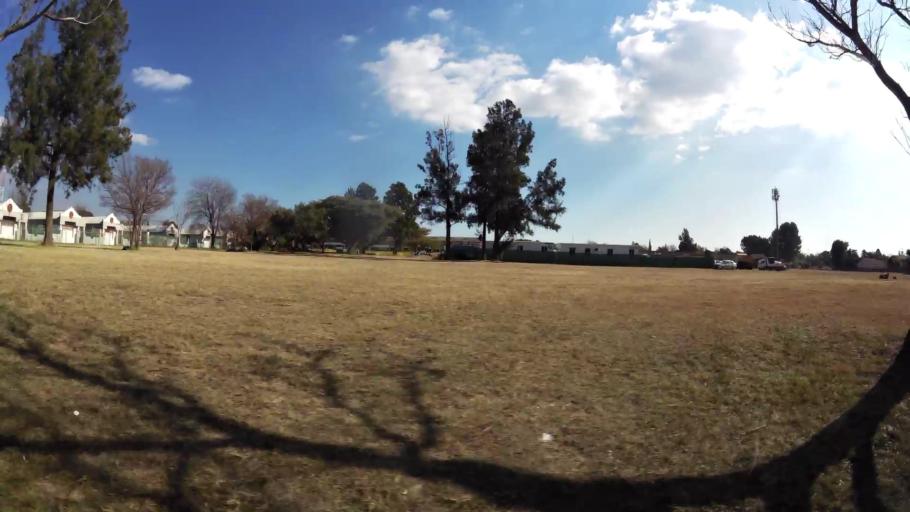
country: ZA
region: Gauteng
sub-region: Ekurhuleni Metropolitan Municipality
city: Benoni
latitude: -26.1461
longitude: 28.3444
